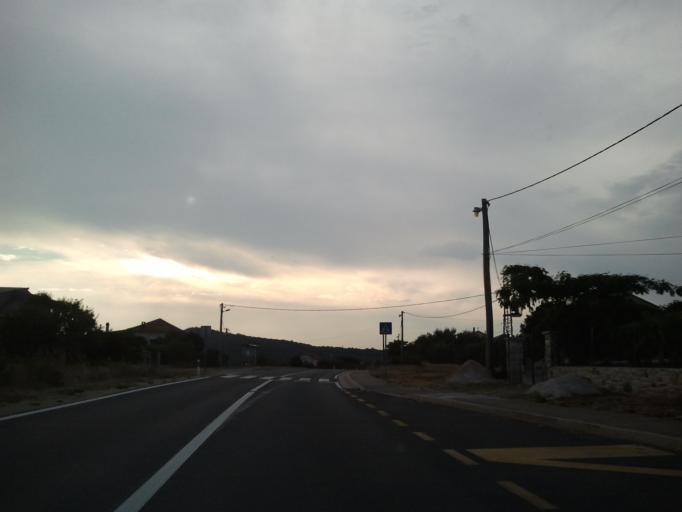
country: HR
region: Zadarska
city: Posedarje
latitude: 44.2208
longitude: 15.4504
